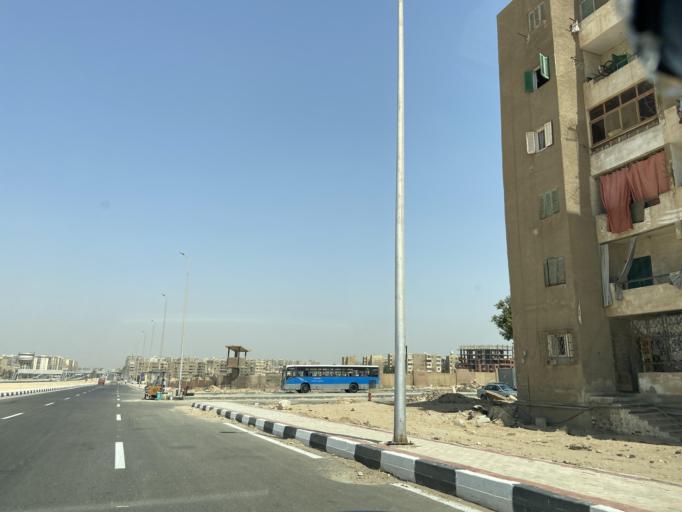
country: EG
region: Muhafazat al Qahirah
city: Cairo
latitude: 30.0390
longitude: 31.3586
